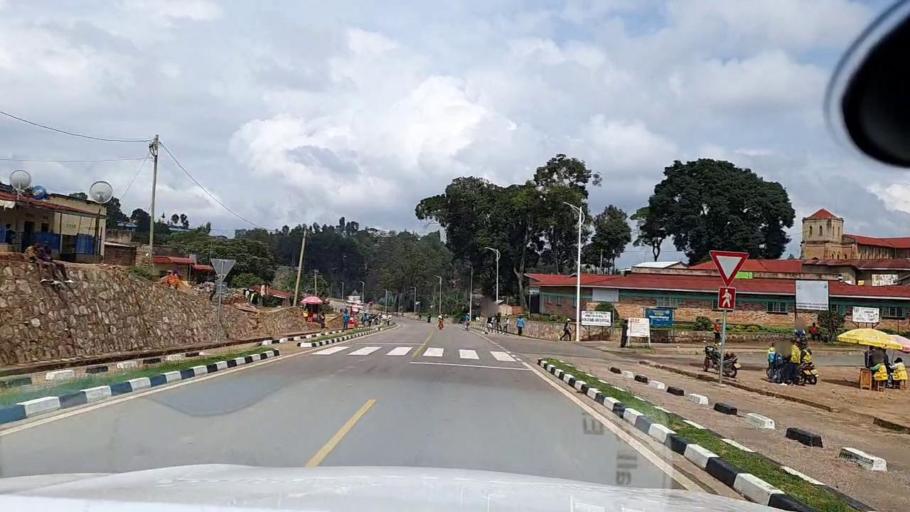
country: RW
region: Southern Province
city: Nzega
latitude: -2.4849
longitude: 29.5288
